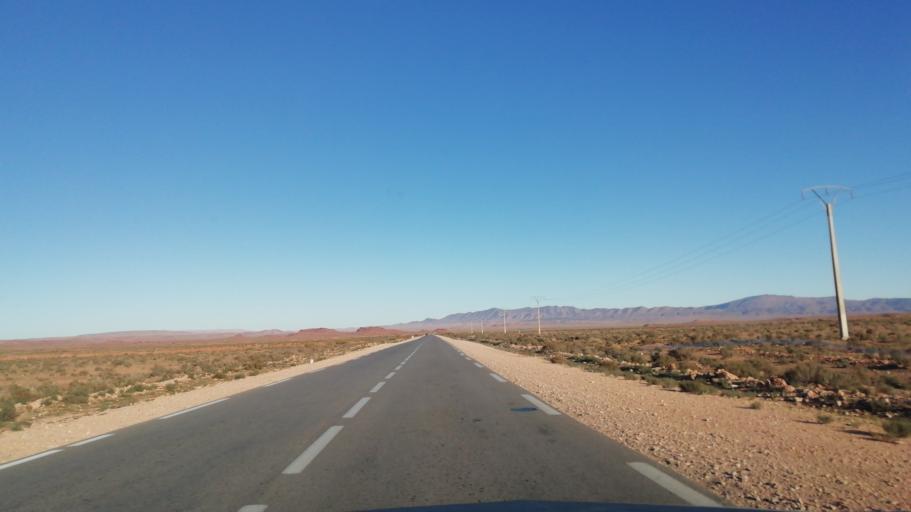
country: DZ
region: El Bayadh
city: El Abiodh Sidi Cheikh
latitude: 33.1679
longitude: 0.4737
